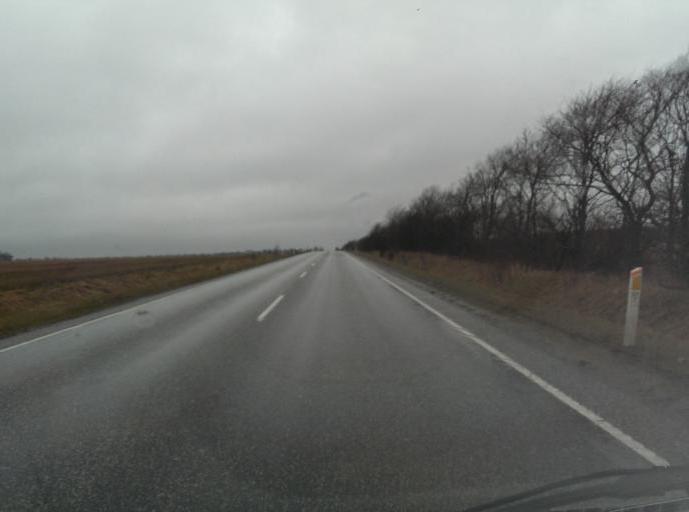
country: DK
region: South Denmark
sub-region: Varde Kommune
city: Varde
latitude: 55.7495
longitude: 8.4935
